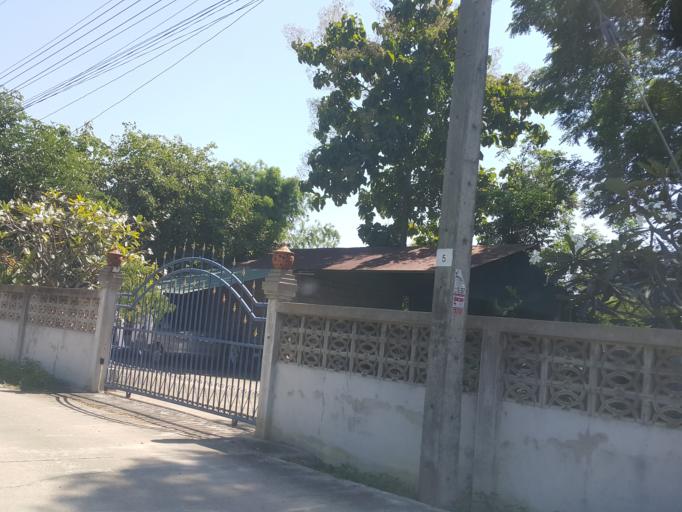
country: TH
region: Chiang Mai
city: Saraphi
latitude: 18.7595
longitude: 99.0547
